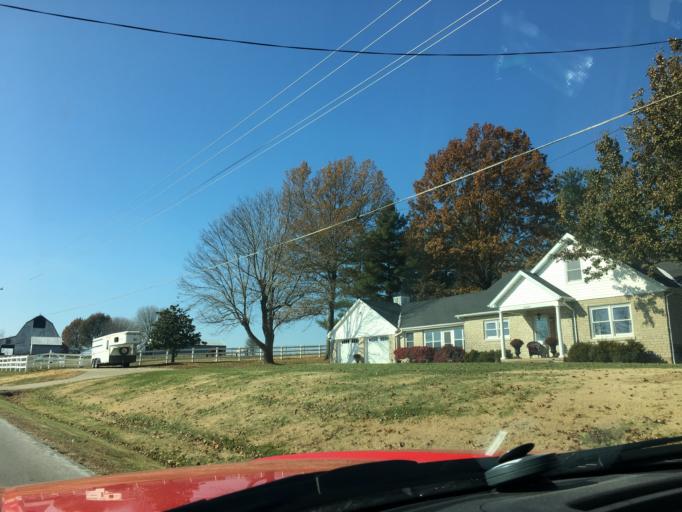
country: US
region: Missouri
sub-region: Cole County
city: Wardsville
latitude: 38.4872
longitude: -92.1812
